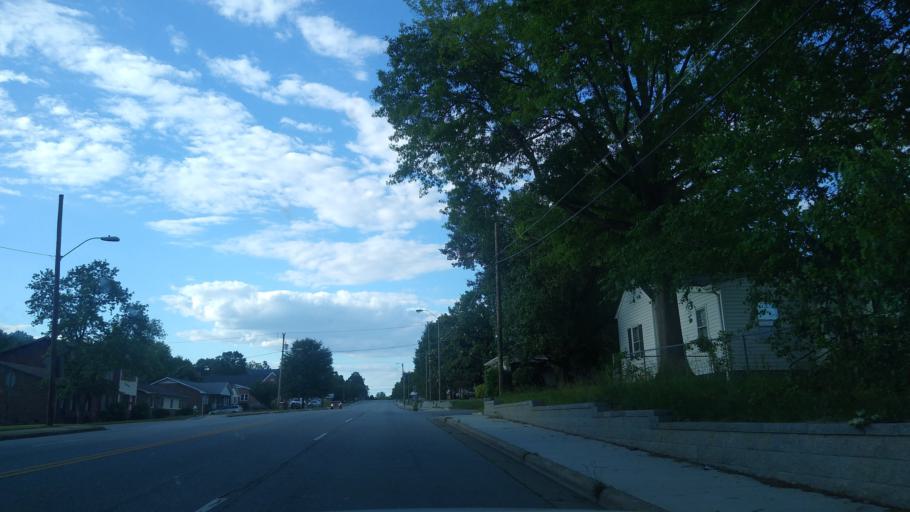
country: US
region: North Carolina
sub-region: Guilford County
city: Greensboro
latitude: 36.1031
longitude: -79.7751
